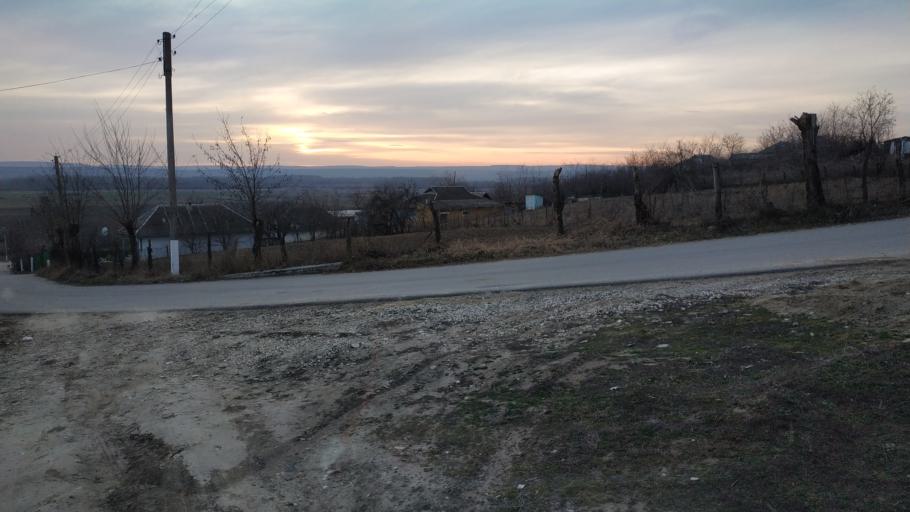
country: MD
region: Hincesti
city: Dancu
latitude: 46.7445
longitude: 28.2107
